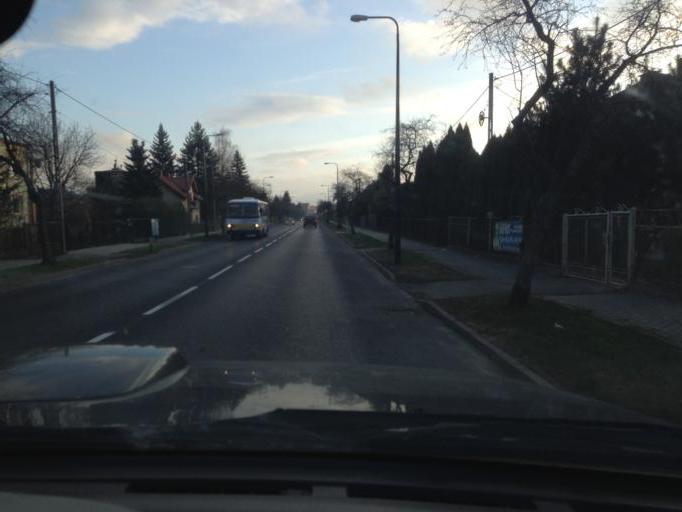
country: PL
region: Subcarpathian Voivodeship
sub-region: Powiat jasielski
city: Jaslo
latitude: 49.7579
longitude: 21.4717
